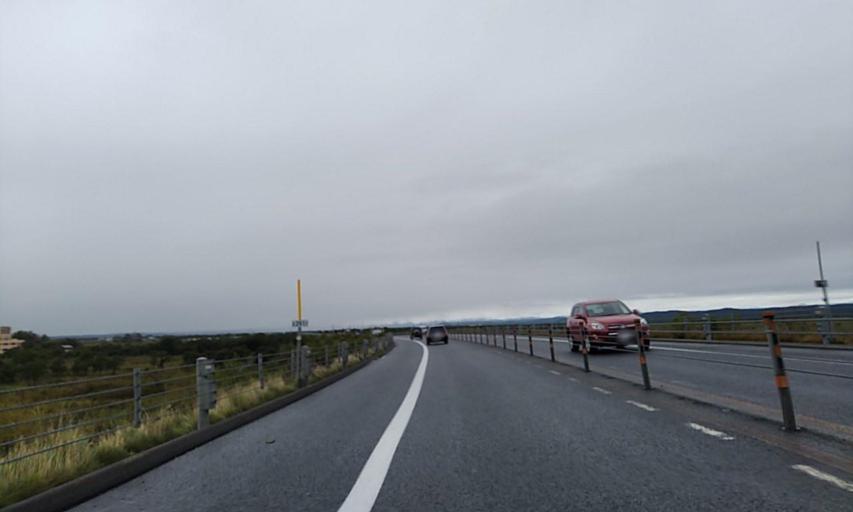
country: JP
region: Hokkaido
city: Kushiro
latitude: 43.0356
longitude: 144.3638
